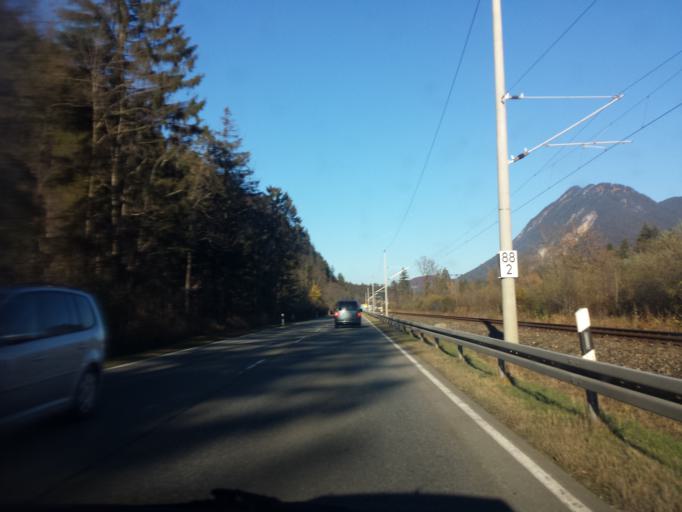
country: DE
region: Bavaria
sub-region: Upper Bavaria
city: Eschenlohe
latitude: 47.5826
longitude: 11.1696
